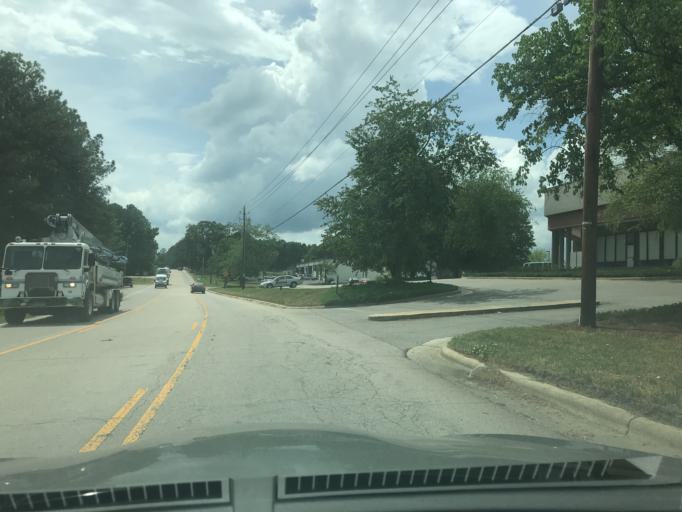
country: US
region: North Carolina
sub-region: Wake County
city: Wake Forest
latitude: 35.8849
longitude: -78.5813
